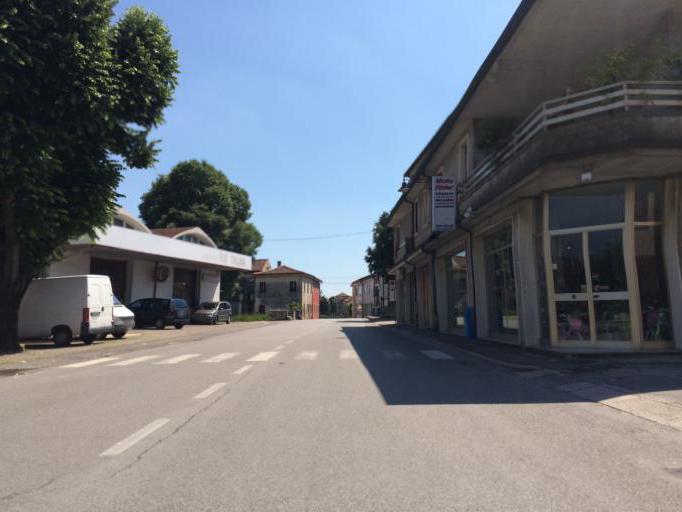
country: IT
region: Veneto
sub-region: Provincia di Vicenza
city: Sossano
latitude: 45.3560
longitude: 11.5062
